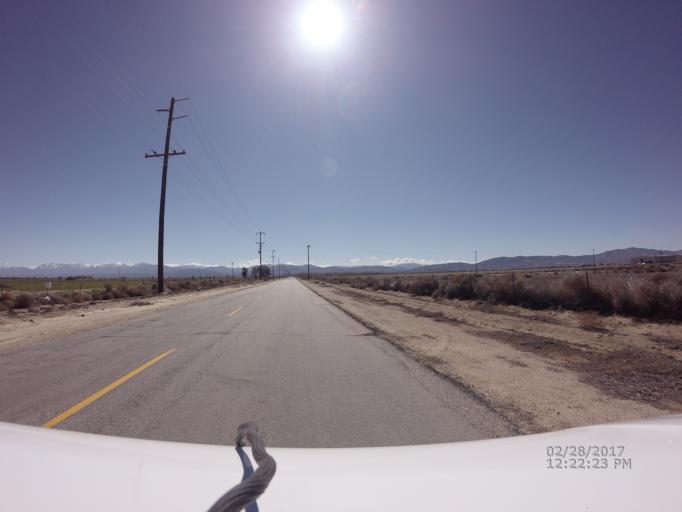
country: US
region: California
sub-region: Los Angeles County
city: Palmdale
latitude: 34.6177
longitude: -118.0587
